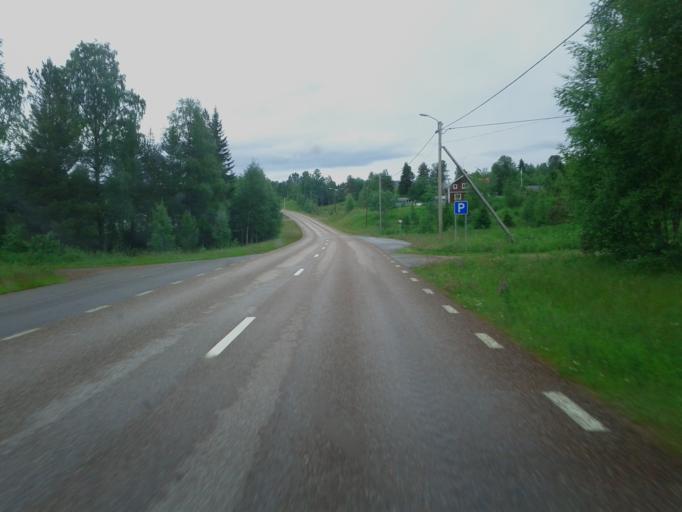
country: NO
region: Hedmark
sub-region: Trysil
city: Innbygda
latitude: 61.7388
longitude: 12.9788
